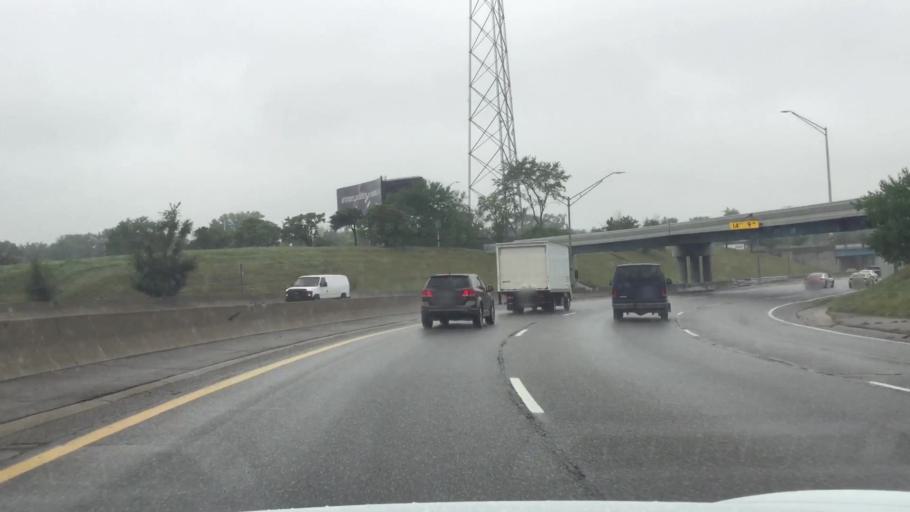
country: US
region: Michigan
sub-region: Wayne County
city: Highland Park
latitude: 42.3852
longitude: -83.1476
